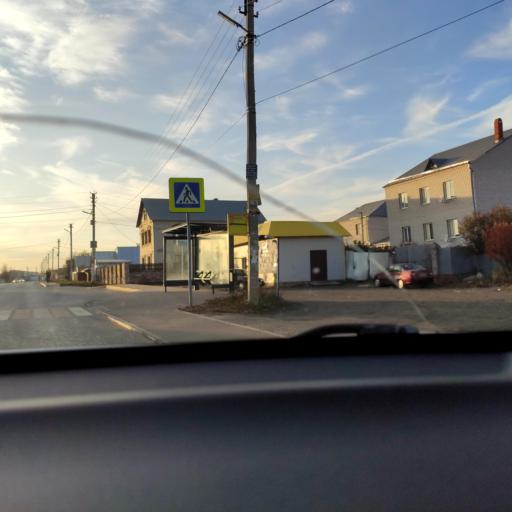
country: RU
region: Tatarstan
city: Staroye Arakchino
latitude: 55.8793
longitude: 49.0473
